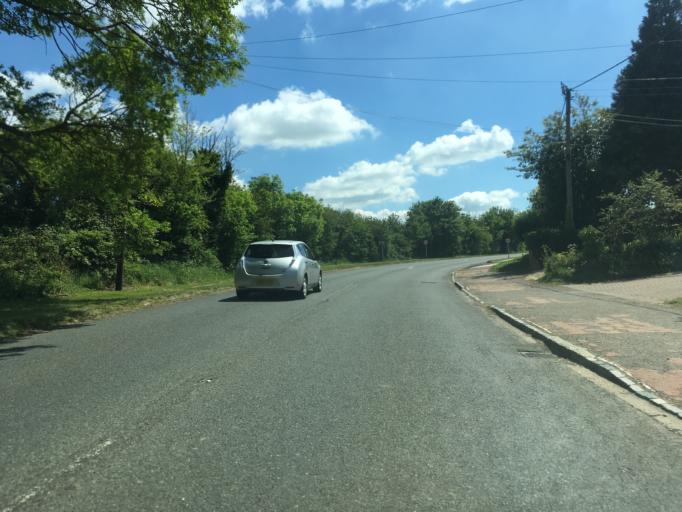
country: GB
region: England
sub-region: Milton Keynes
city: Wavendon
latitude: 52.0262
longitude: -0.6673
